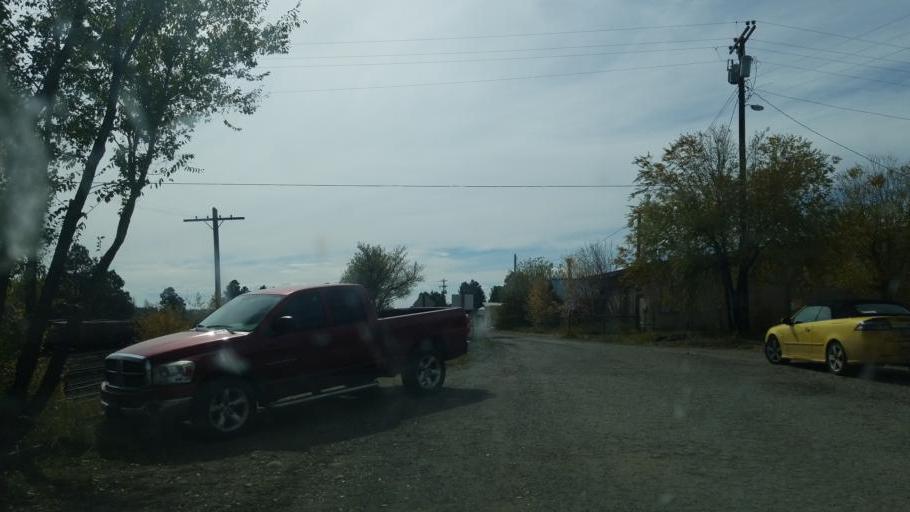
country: US
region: New Mexico
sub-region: Rio Arriba County
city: Chama
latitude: 36.9018
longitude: -106.5791
